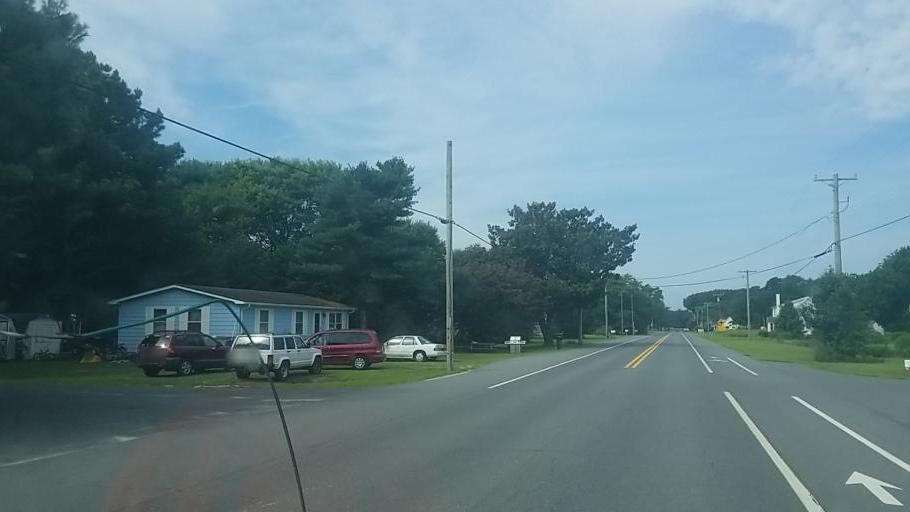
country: US
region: Delaware
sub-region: Sussex County
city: Ocean View
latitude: 38.5475
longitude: -75.1578
